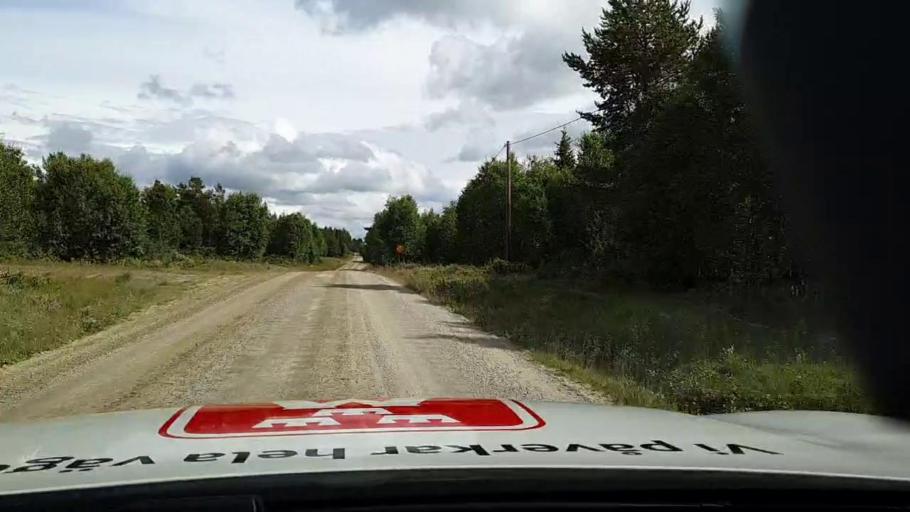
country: SE
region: Jaemtland
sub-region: Are Kommun
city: Jarpen
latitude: 62.5524
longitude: 13.4420
